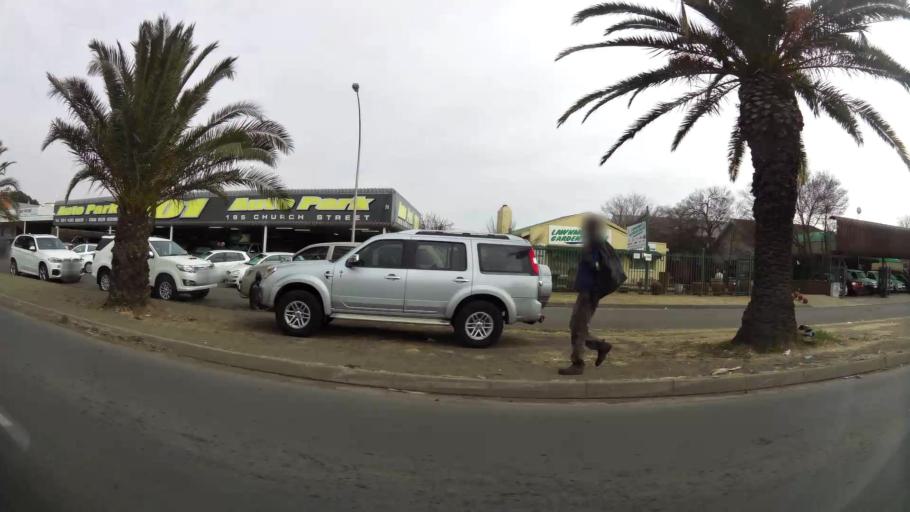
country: ZA
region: Orange Free State
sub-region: Mangaung Metropolitan Municipality
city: Bloemfontein
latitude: -29.1337
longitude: 26.2174
